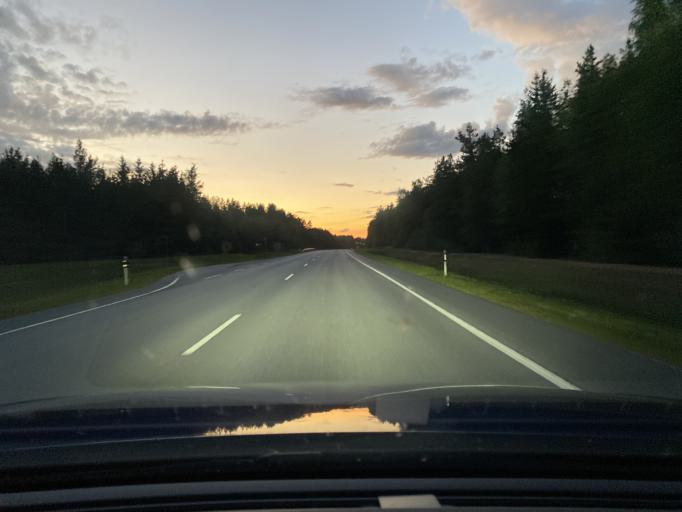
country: FI
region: Varsinais-Suomi
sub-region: Loimaa
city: Oripaeae
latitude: 60.9237
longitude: 22.6860
